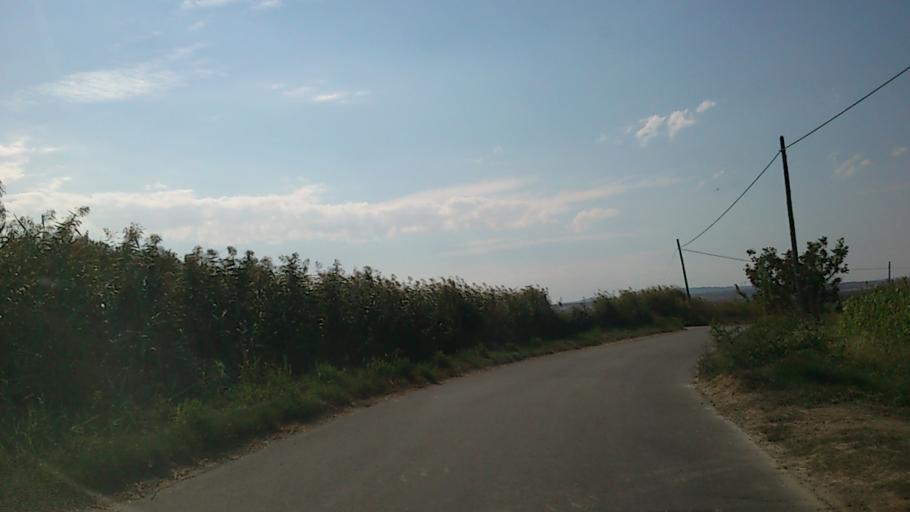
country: ES
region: Aragon
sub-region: Provincia de Zaragoza
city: Puebla de Alfinden
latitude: 41.6231
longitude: -0.7571
